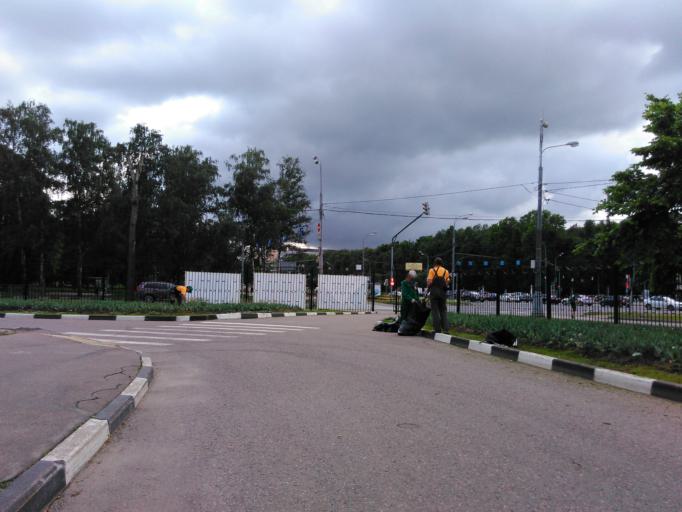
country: RU
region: Moscow
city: Luzhniki
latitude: 55.7009
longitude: 37.5477
